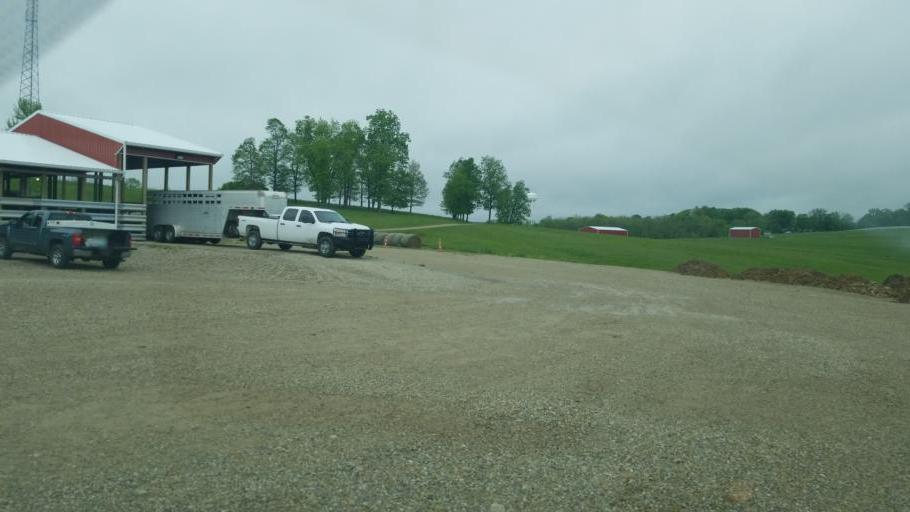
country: US
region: Ohio
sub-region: Highland County
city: Hillsboro
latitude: 39.2165
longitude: -83.5940
